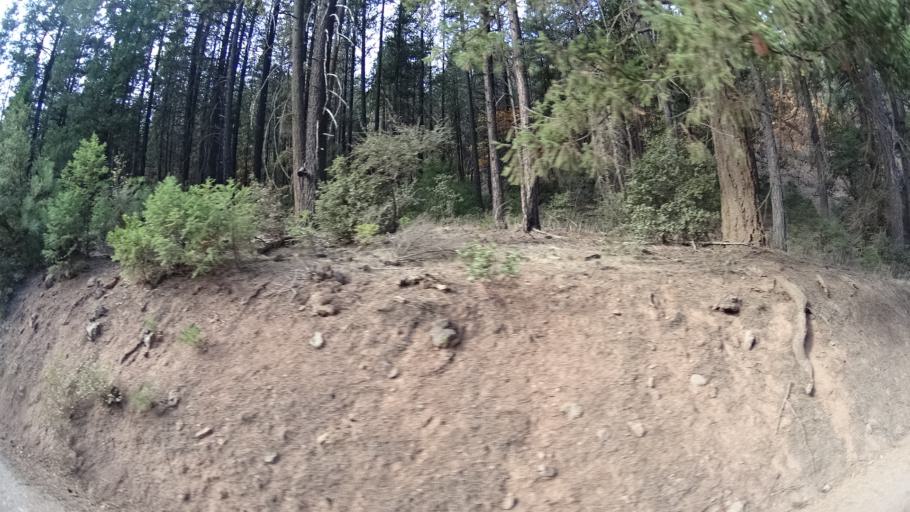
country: US
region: California
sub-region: Siskiyou County
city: Yreka
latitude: 41.6925
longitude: -122.8186
